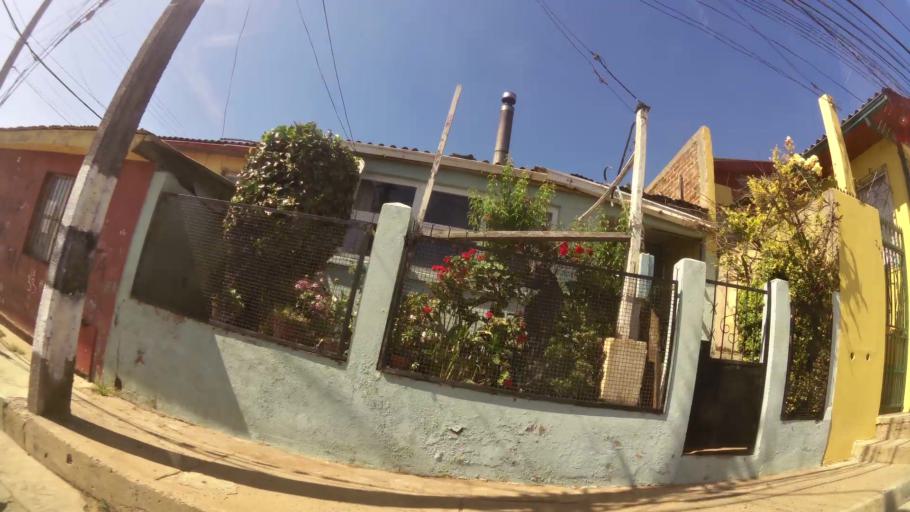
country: CL
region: Valparaiso
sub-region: Provincia de Valparaiso
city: Valparaiso
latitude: -33.0461
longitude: -71.6476
